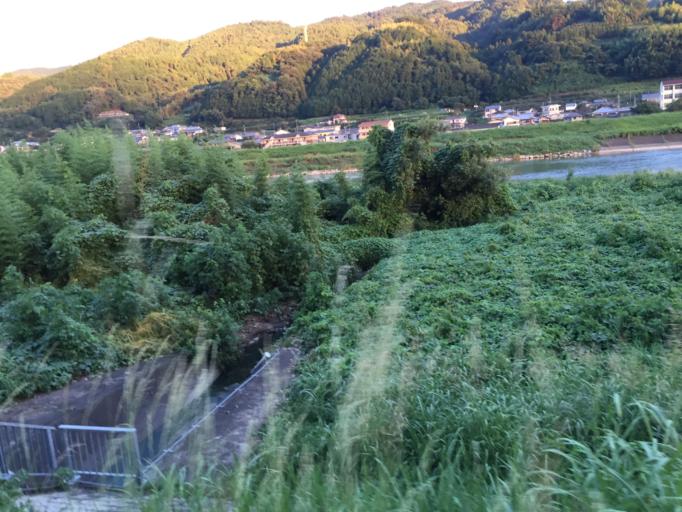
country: JP
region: Wakayama
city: Hashimoto
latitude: 34.3118
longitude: 135.6061
